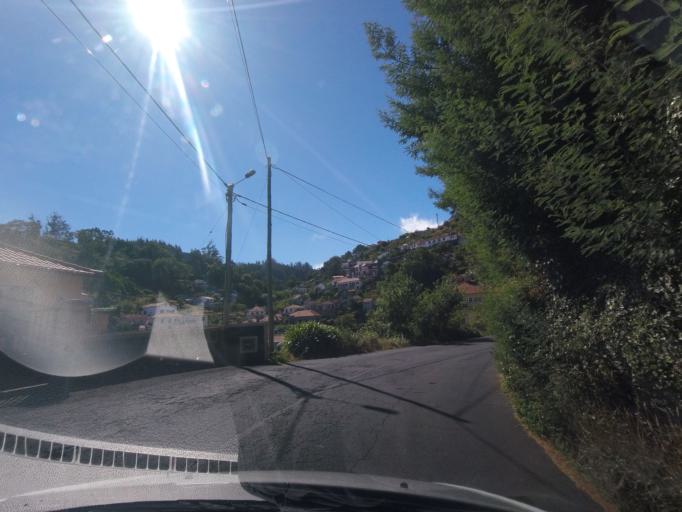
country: PT
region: Madeira
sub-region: Santa Cruz
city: Camacha
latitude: 32.6870
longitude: -16.8514
